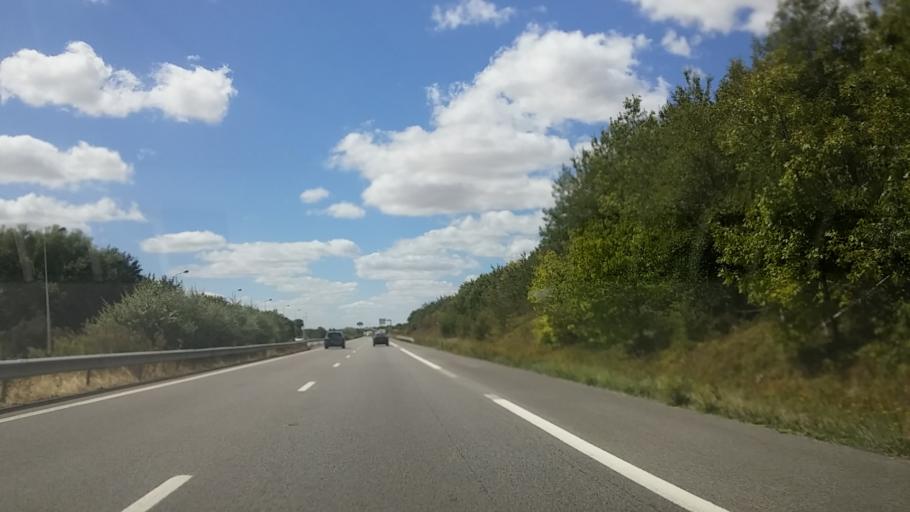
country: FR
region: Ile-de-France
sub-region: Departement des Yvelines
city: Bazainville
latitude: 48.7932
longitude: 1.6437
